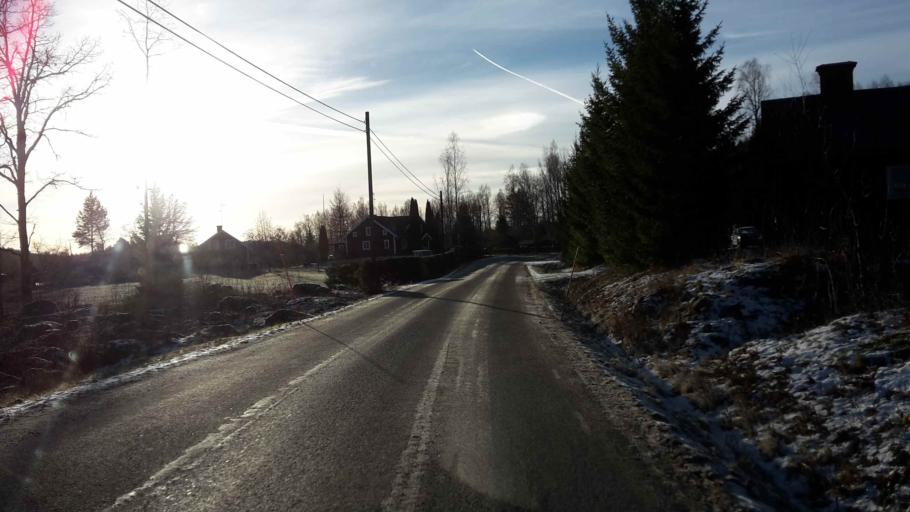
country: SE
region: OEstergoetland
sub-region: Atvidabergs Kommun
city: Atvidaberg
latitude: 58.2471
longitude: 16.1002
